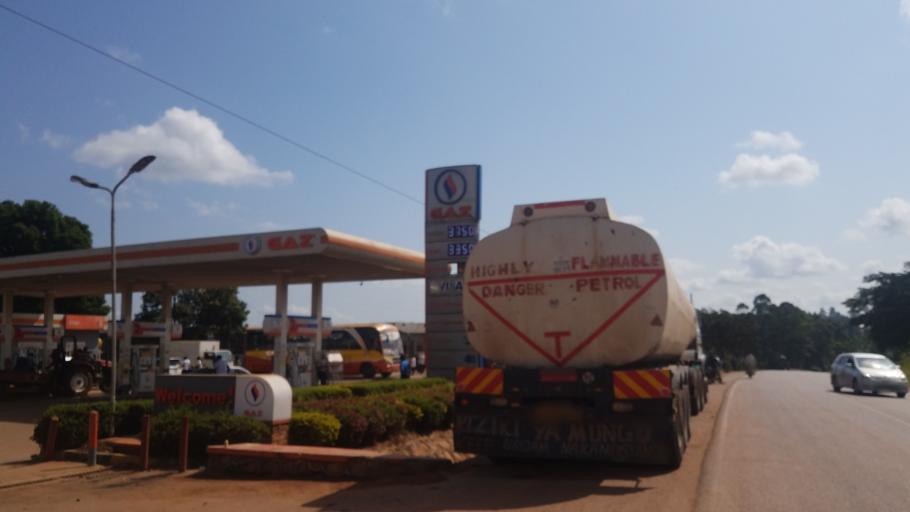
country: UG
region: Central Region
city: Masaka
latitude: -0.3324
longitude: 31.7209
